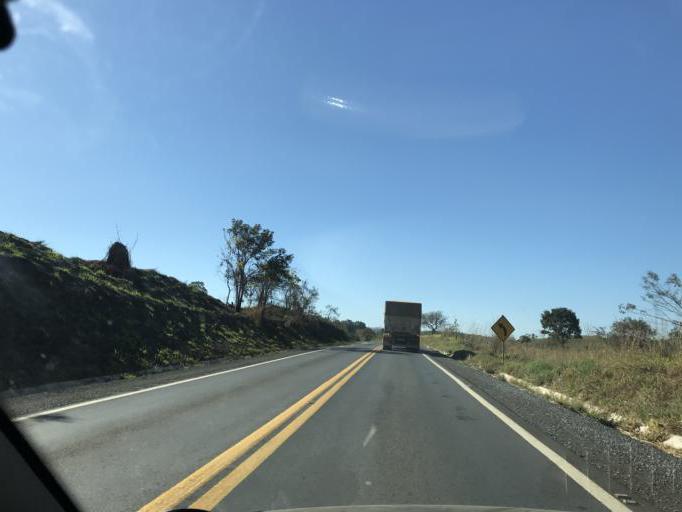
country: BR
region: Minas Gerais
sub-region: Bambui
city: Bambui
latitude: -19.8683
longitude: -45.9860
